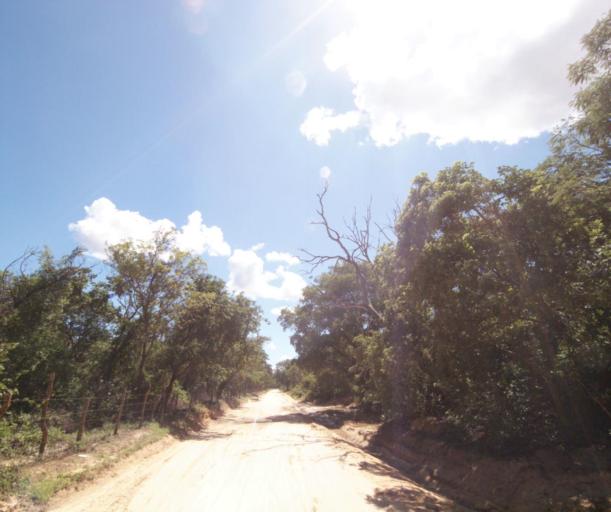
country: BR
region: Bahia
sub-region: Carinhanha
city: Carinhanha
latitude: -14.2308
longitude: -44.3057
